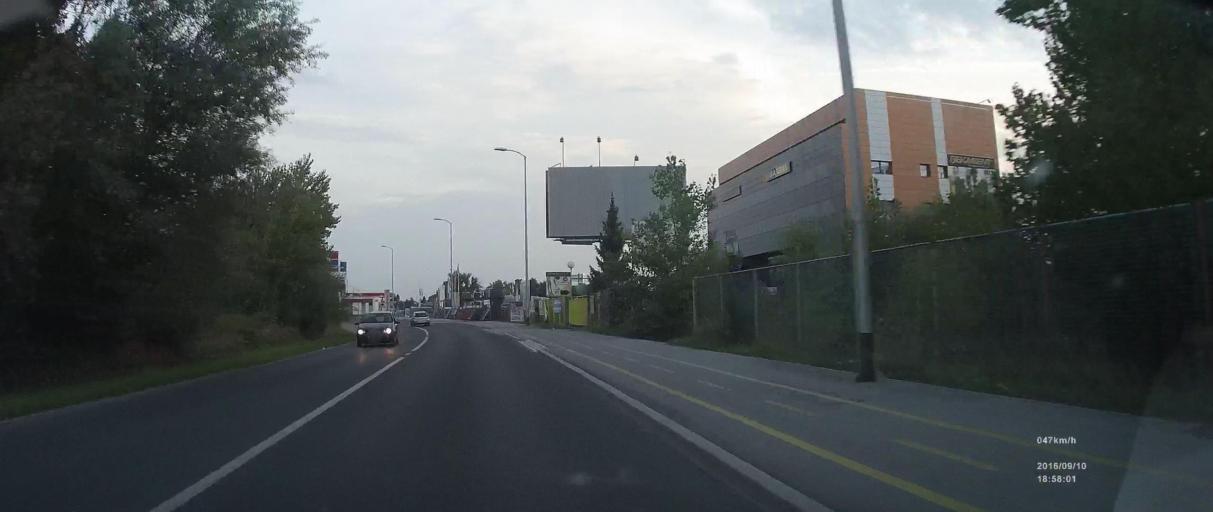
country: HR
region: Grad Zagreb
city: Novi Zagreb
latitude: 45.7629
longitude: 15.9810
